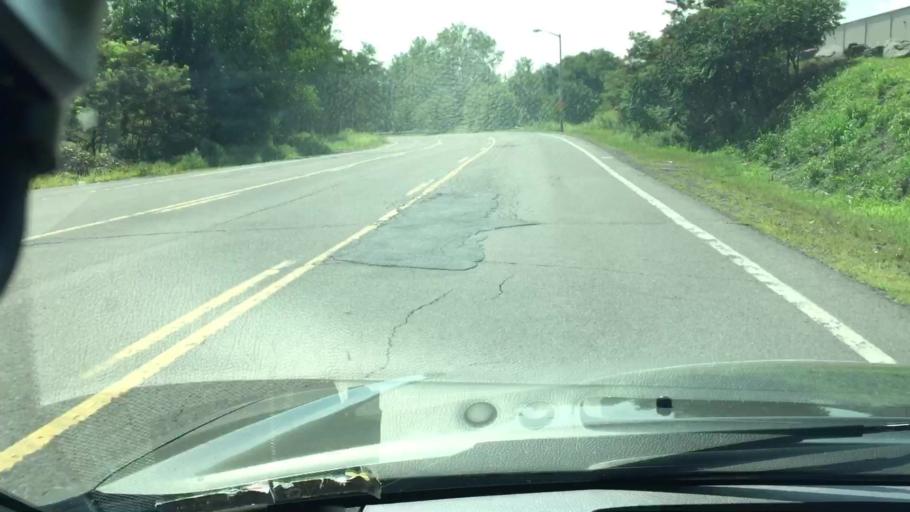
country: US
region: Pennsylvania
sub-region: Luzerne County
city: Plymouth
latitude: 41.1994
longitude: -75.9406
